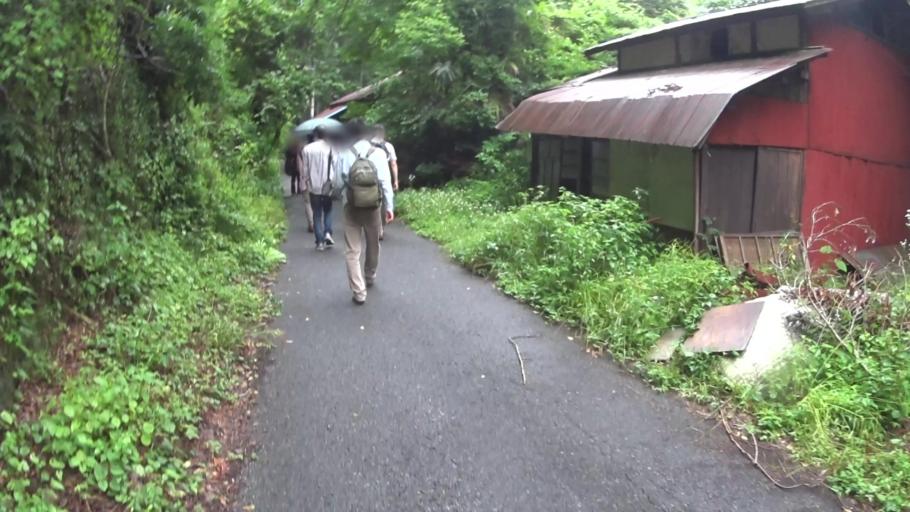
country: JP
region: Tokyo
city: Itsukaichi
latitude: 35.7942
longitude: 139.0629
